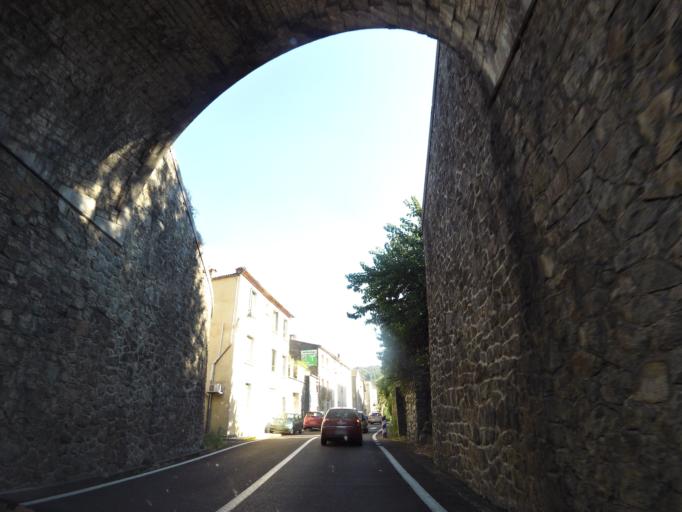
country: FR
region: Languedoc-Roussillon
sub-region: Departement du Gard
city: Sumene
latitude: 43.9983
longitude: 3.6765
